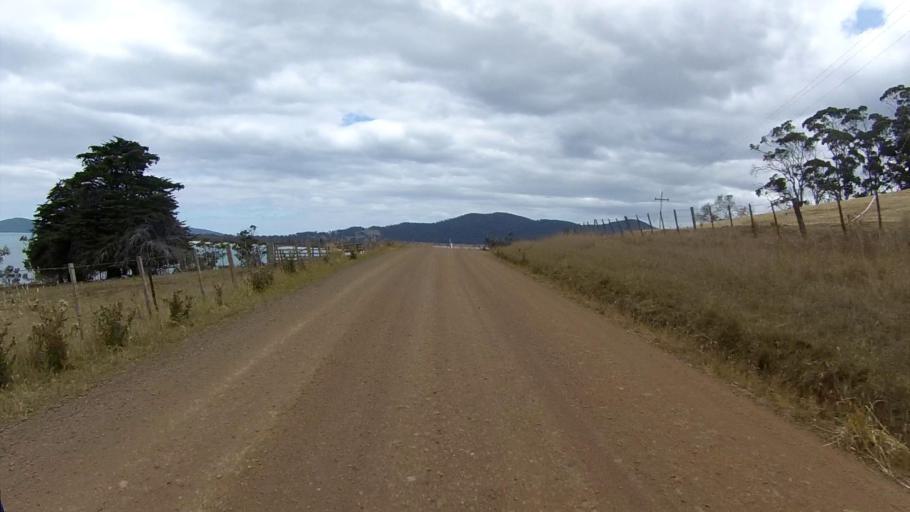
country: AU
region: Tasmania
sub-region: Sorell
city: Sorell
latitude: -42.6255
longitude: 147.9331
